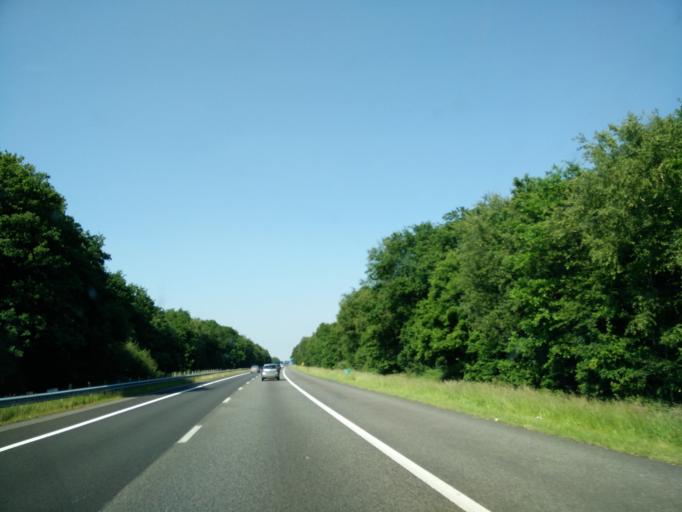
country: NL
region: Drenthe
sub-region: Gemeente Hoogeveen
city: Hoogeveen
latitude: 52.7907
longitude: 6.4496
